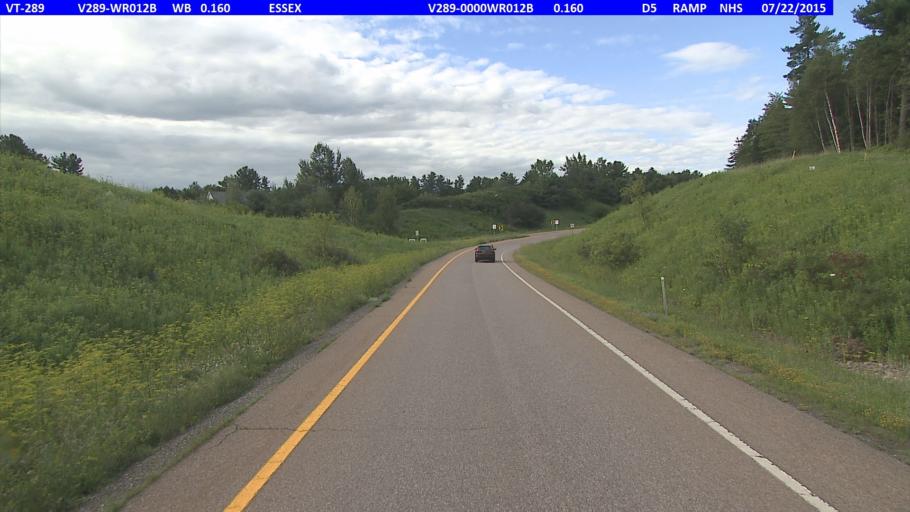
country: US
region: Vermont
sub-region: Chittenden County
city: Essex Junction
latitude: 44.4824
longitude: -73.0675
